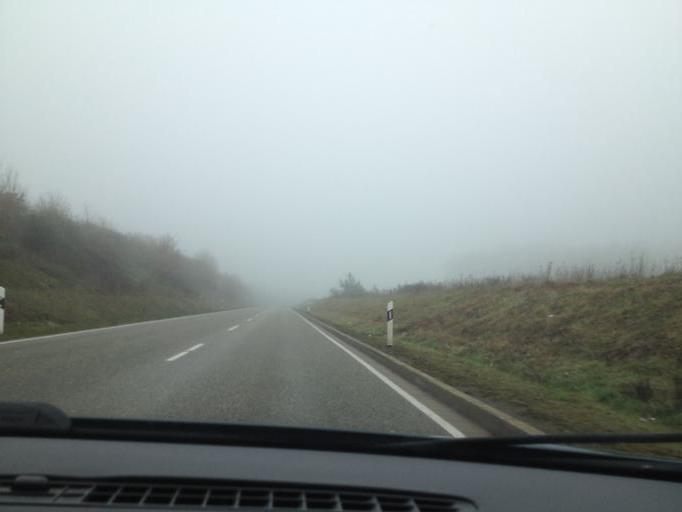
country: DE
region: Rheinland-Pfalz
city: Mackenbach
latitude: 49.4704
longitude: 7.5941
